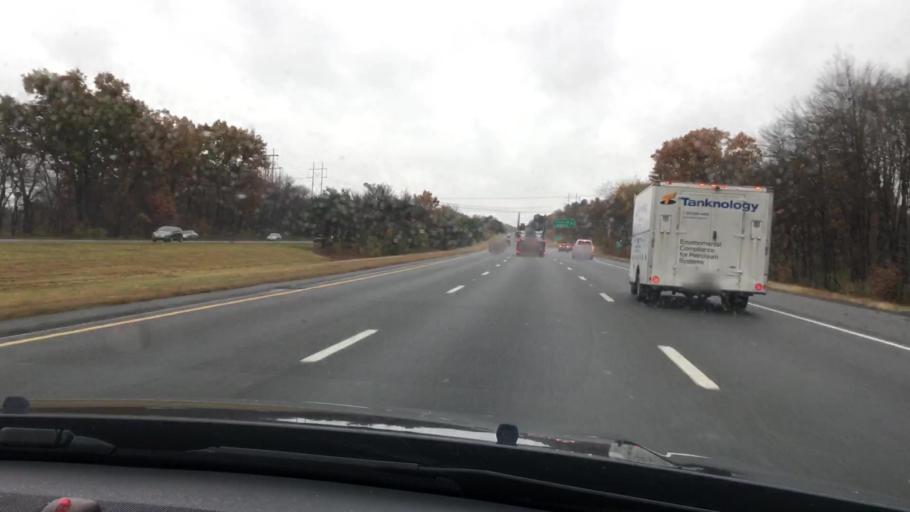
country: US
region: Massachusetts
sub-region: Middlesex County
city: Westford
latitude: 42.5733
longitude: -71.4208
